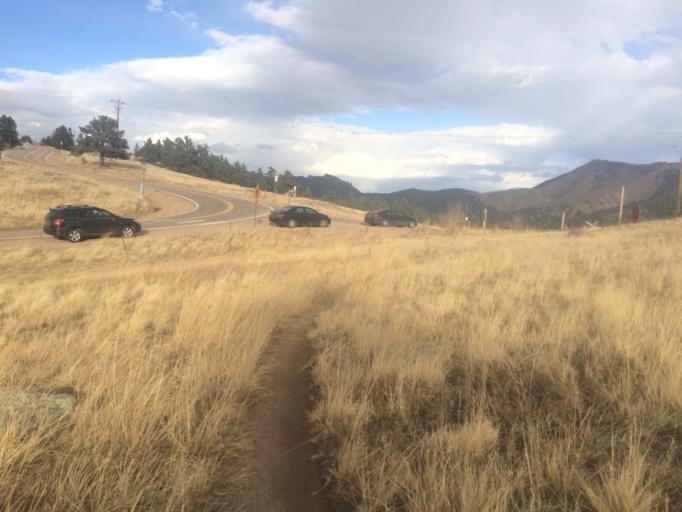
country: US
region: Colorado
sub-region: Boulder County
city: Coal Creek
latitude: 39.9536
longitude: -105.3383
